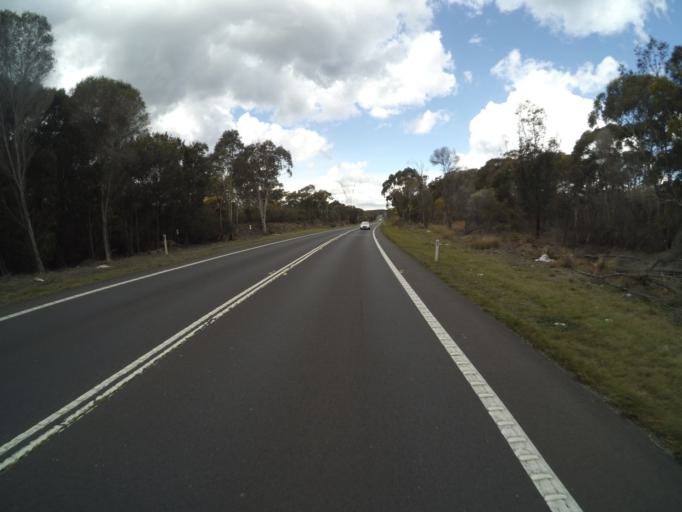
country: AU
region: New South Wales
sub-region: Wollondilly
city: Douglas Park
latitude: -34.2936
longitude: 150.7333
